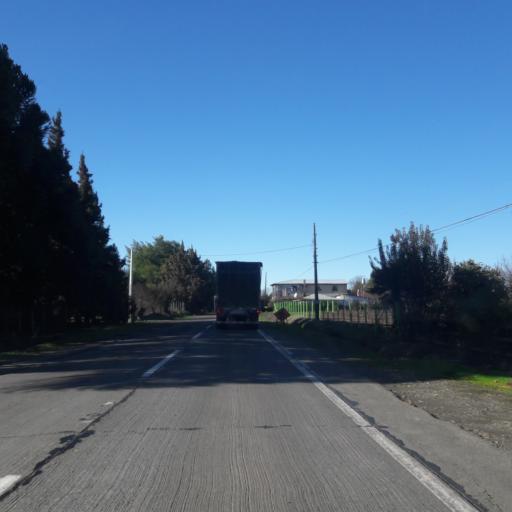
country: CL
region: Araucania
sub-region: Provincia de Malleco
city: Angol
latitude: -37.7763
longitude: -72.5419
